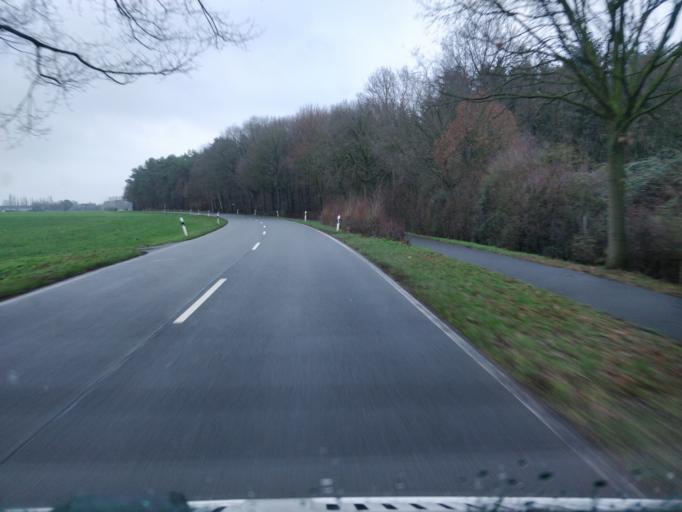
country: DE
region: North Rhine-Westphalia
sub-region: Regierungsbezirk Dusseldorf
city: Mehrhoog
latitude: 51.7505
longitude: 6.5357
